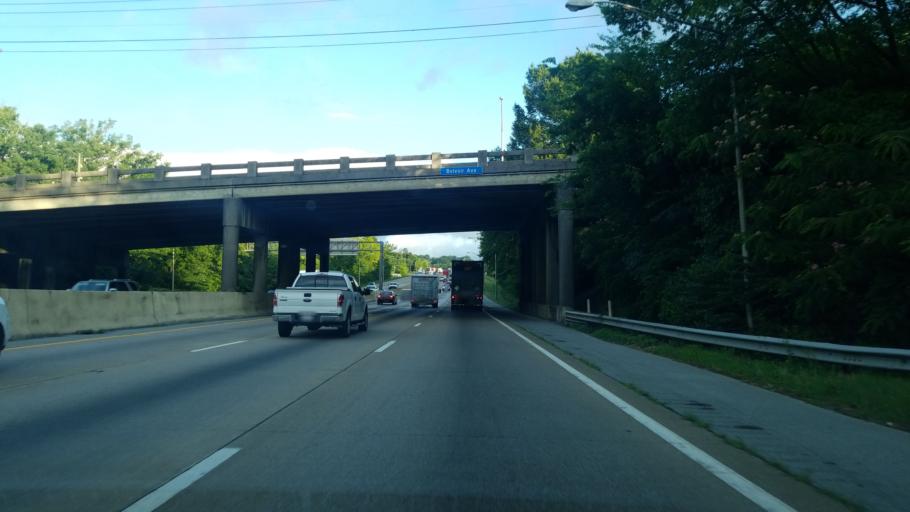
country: US
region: Tennessee
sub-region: Hamilton County
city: East Ridge
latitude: 35.0109
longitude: -85.2433
